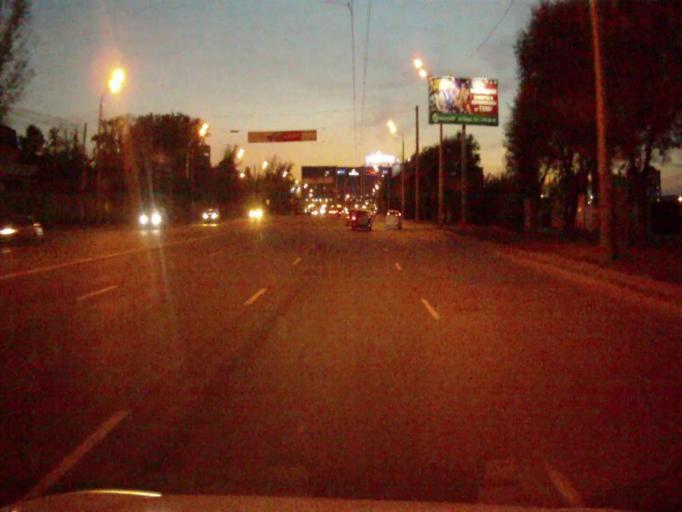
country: RU
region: Chelyabinsk
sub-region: Gorod Chelyabinsk
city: Chelyabinsk
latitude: 55.1710
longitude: 61.3644
